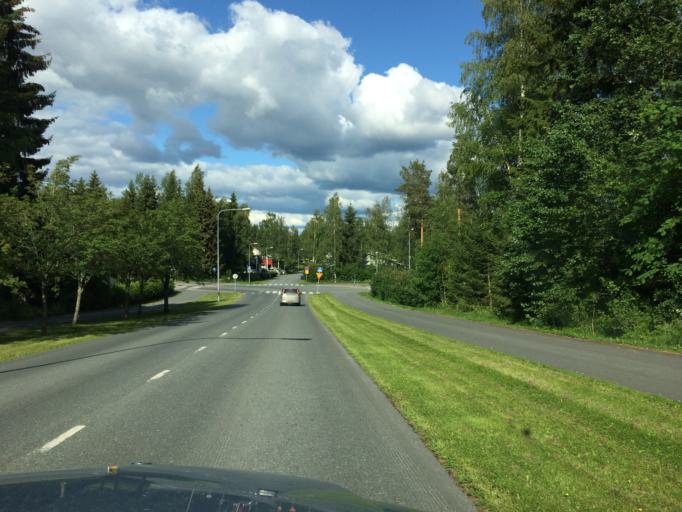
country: FI
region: Haeme
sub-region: Haemeenlinna
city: Parola
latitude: 60.9819
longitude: 24.3822
